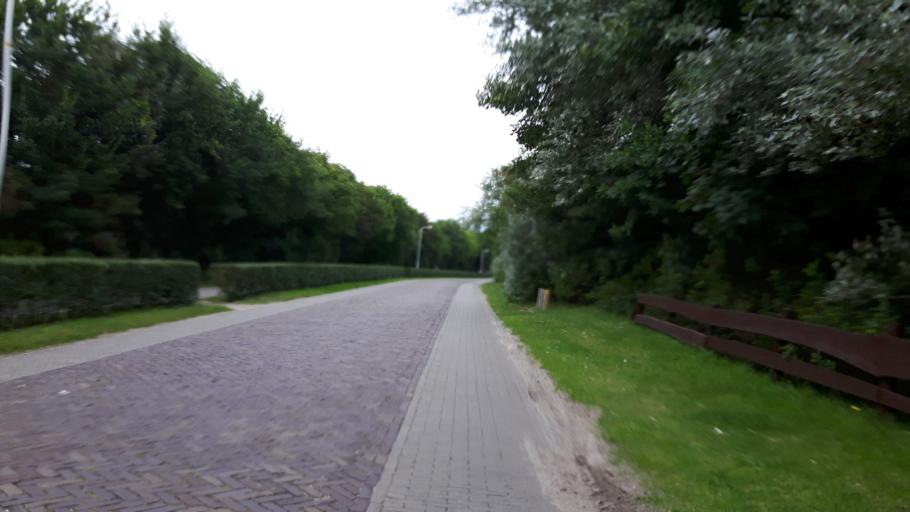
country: NL
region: Friesland
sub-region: Gemeente Ameland
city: Nes
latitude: 53.4535
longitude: 5.7767
